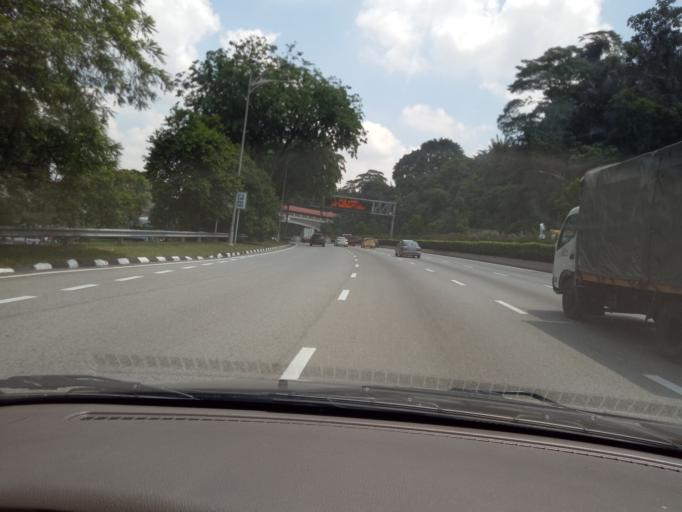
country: MY
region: Kuala Lumpur
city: Kuala Lumpur
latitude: 3.1381
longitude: 101.6897
